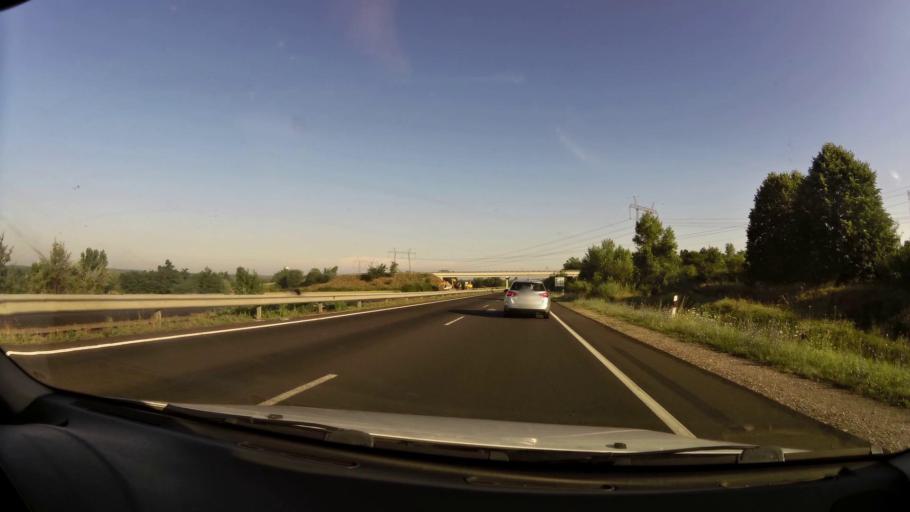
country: HU
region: Pest
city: Cegledbercel
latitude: 47.2338
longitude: 19.6689
